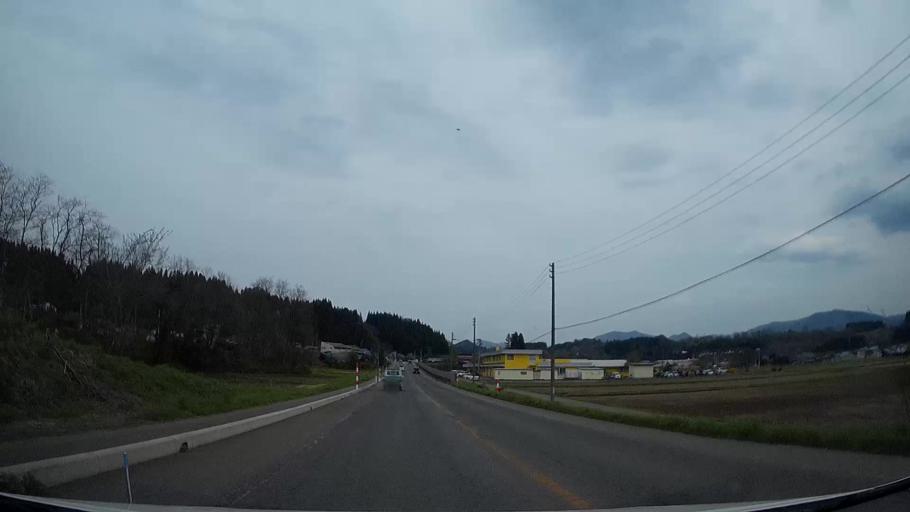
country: JP
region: Akita
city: Hanawa
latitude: 40.2726
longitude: 140.7893
